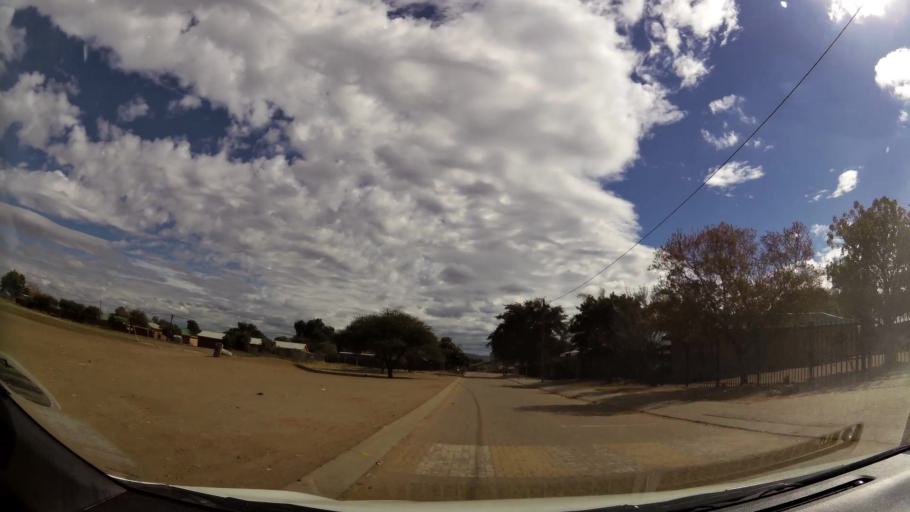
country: ZA
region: Limpopo
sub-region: Waterberg District Municipality
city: Bela-Bela
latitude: -24.8897
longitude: 28.3100
